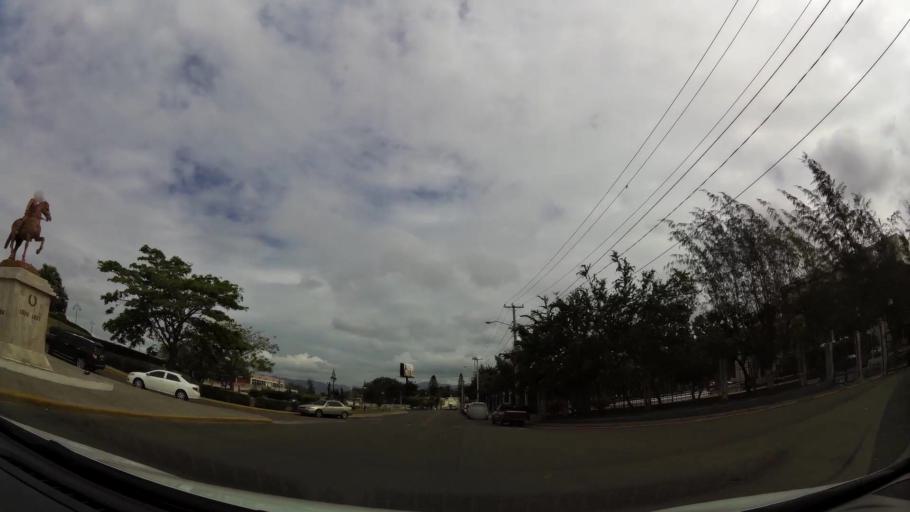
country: DO
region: Santiago
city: Santiago de los Caballeros
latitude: 19.4504
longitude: -70.6933
